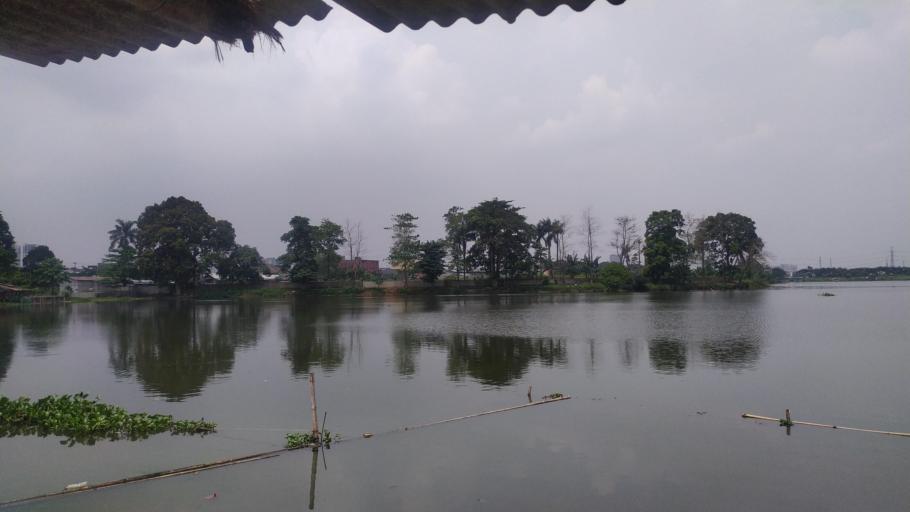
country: ID
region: Banten
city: Tangerang
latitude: -6.2326
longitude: 106.6162
